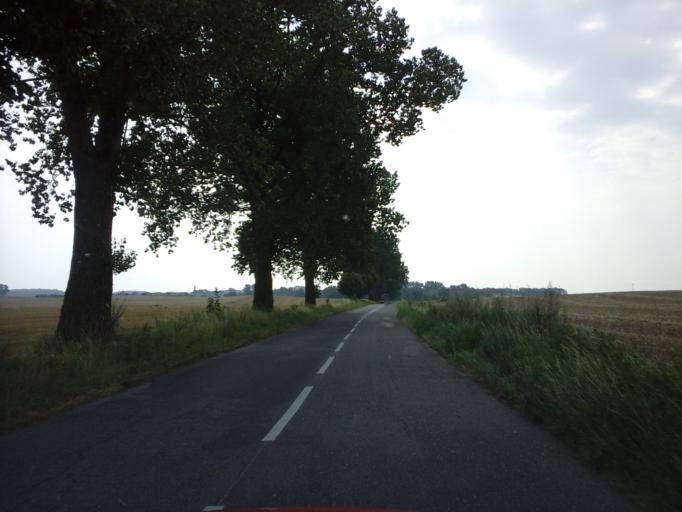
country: PL
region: West Pomeranian Voivodeship
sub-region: Powiat choszczenski
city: Pelczyce
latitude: 53.0546
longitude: 15.3660
